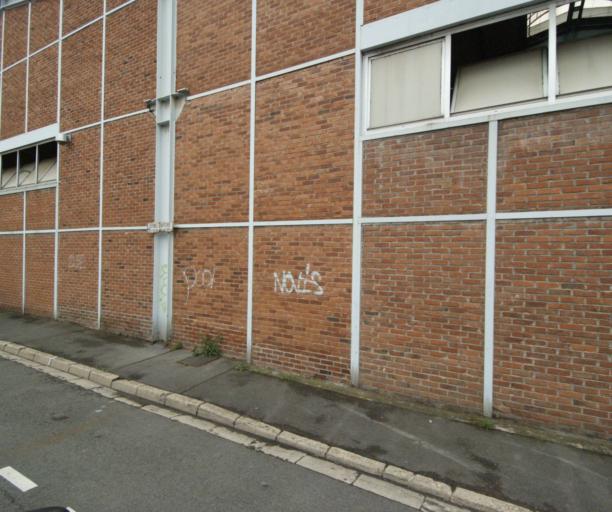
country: FR
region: Nord-Pas-de-Calais
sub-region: Departement du Nord
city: Ronchin
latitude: 50.6078
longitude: 3.0854
